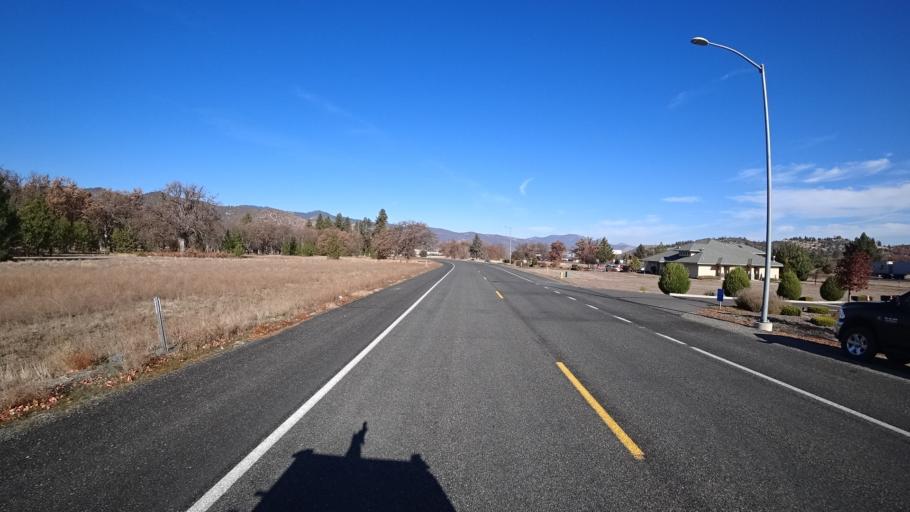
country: US
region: California
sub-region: Siskiyou County
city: Yreka
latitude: 41.6925
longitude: -122.6401
